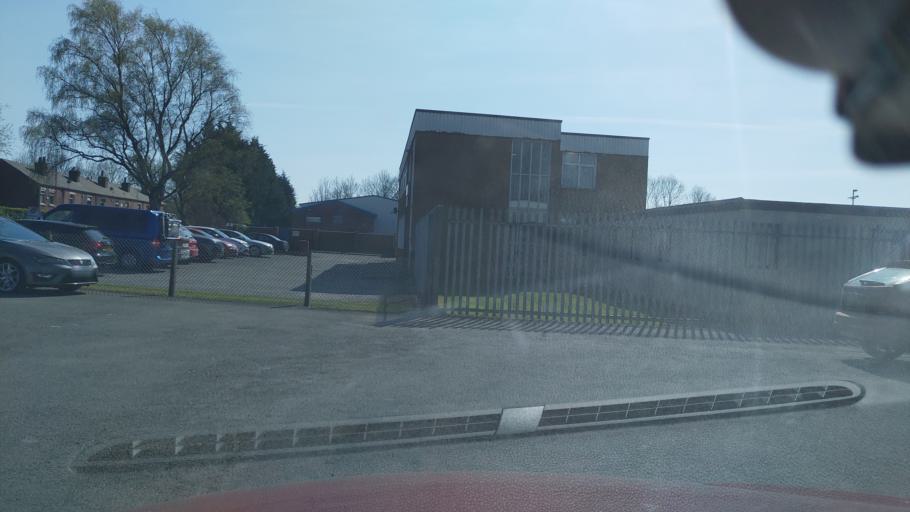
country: GB
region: England
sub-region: Borough of Bolton
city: Horwich
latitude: 53.5943
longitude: -2.5640
